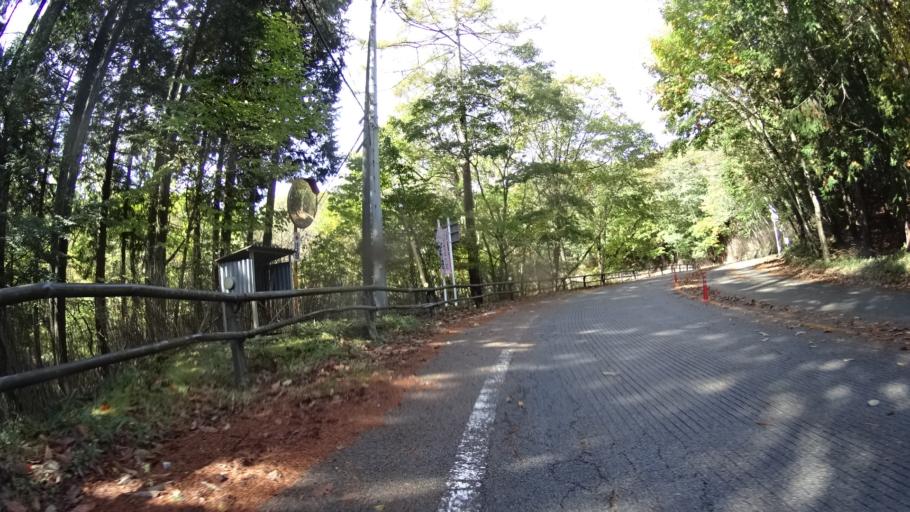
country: JP
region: Yamanashi
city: Enzan
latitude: 35.7890
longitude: 138.8014
